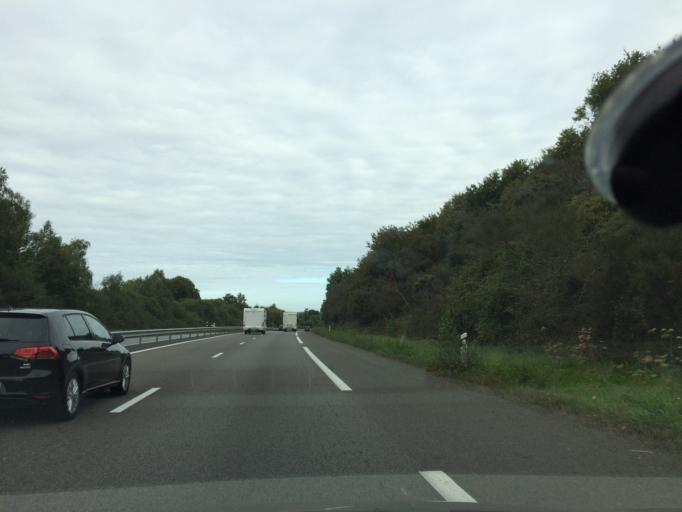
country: FR
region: Brittany
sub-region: Departement d'Ille-et-Vilaine
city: Saint-Pierre-de-Plesguen
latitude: 48.4377
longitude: -1.9231
